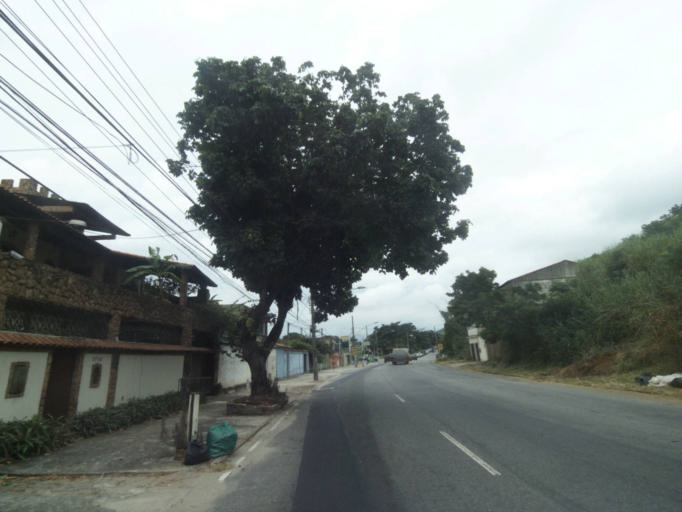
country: BR
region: Rio de Janeiro
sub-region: Nilopolis
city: Nilopolis
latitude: -22.8910
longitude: -43.3922
